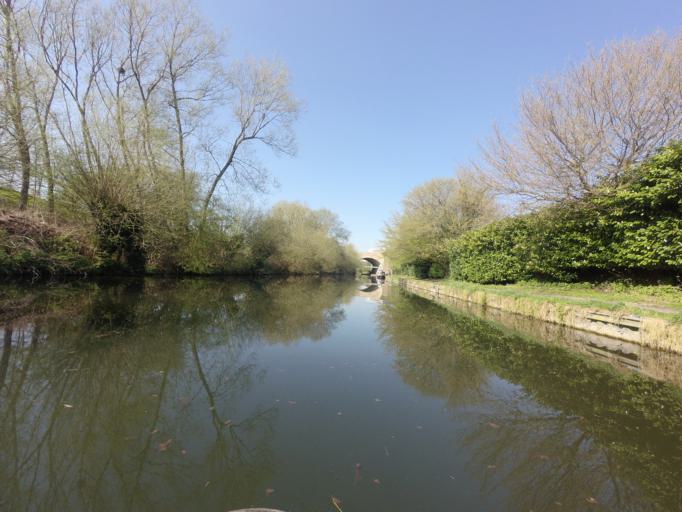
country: GB
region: England
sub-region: Hertfordshire
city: Kings Langley
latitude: 51.7230
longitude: -0.4499
